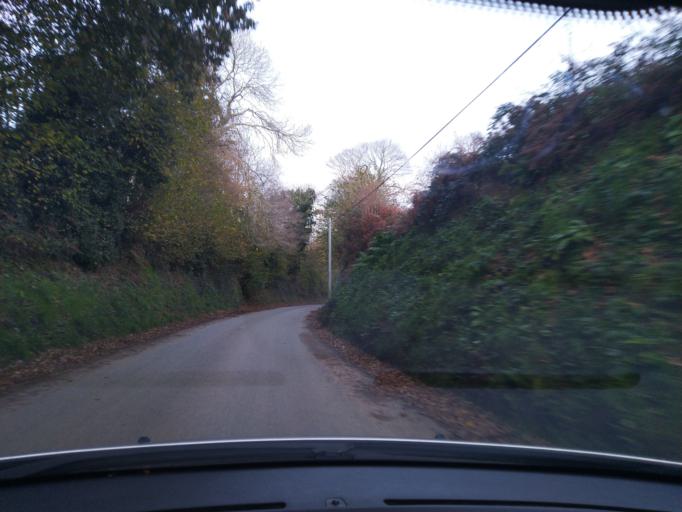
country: FR
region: Brittany
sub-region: Departement du Finistere
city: Guerlesquin
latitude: 48.5539
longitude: -3.6199
